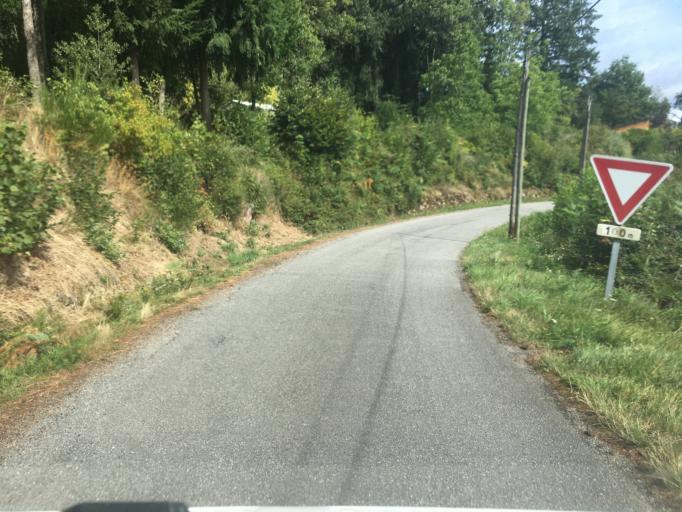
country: FR
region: Auvergne
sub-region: Departement du Cantal
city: Champagnac
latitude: 45.4283
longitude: 2.4124
